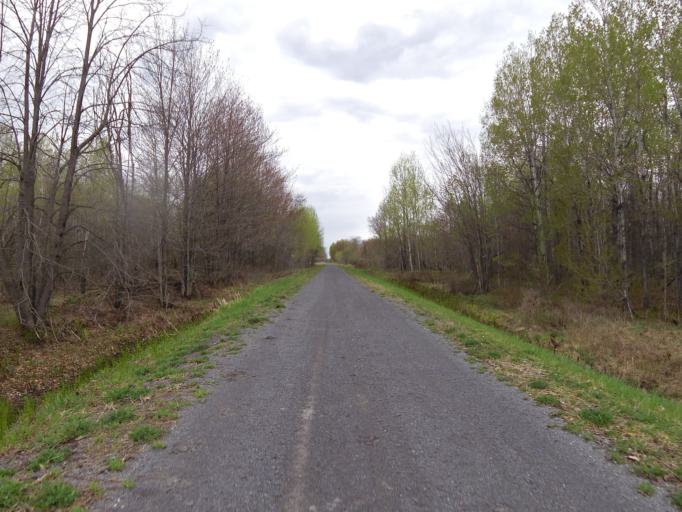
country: CA
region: Quebec
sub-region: Outaouais
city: Papineauville
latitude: 45.5178
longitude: -74.9514
